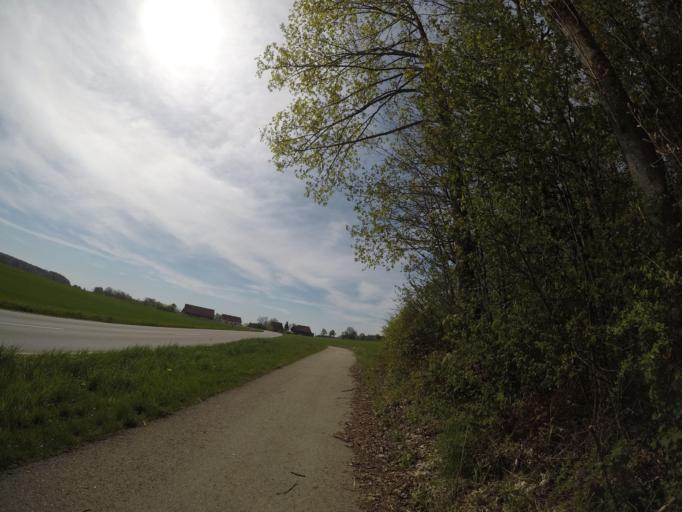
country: DE
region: Baden-Wuerttemberg
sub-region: Tuebingen Region
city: Boms
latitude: 47.9619
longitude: 9.5060
